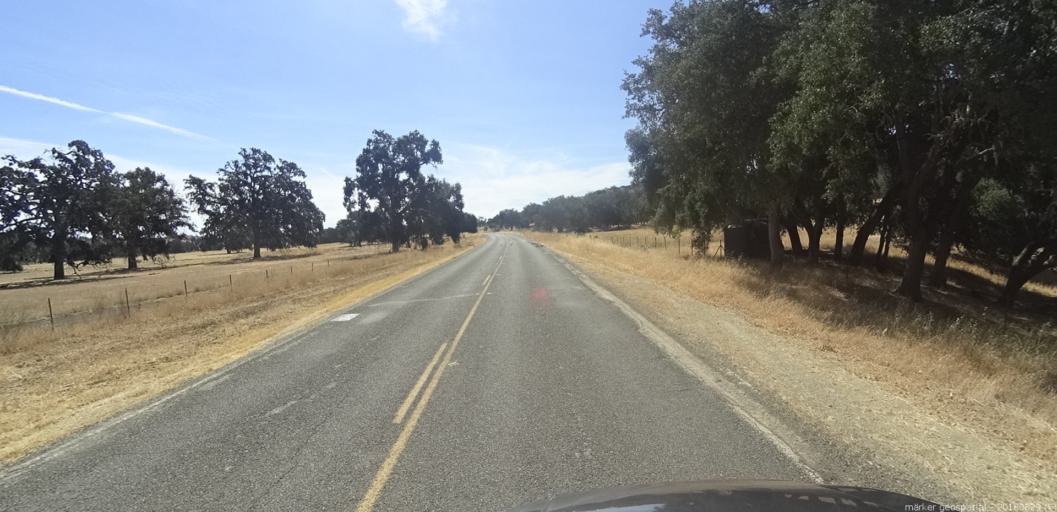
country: US
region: California
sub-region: San Luis Obispo County
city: Lake Nacimiento
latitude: 35.8299
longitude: -121.0228
